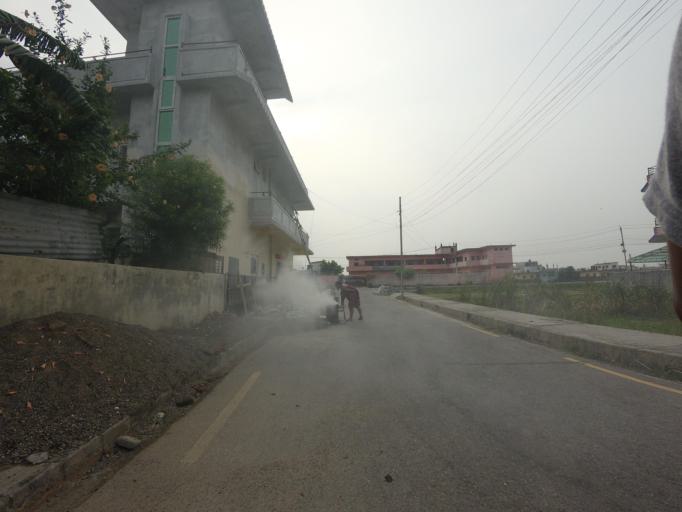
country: NP
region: Western Region
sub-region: Lumbini Zone
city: Bhairahawa
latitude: 27.4969
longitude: 83.4518
